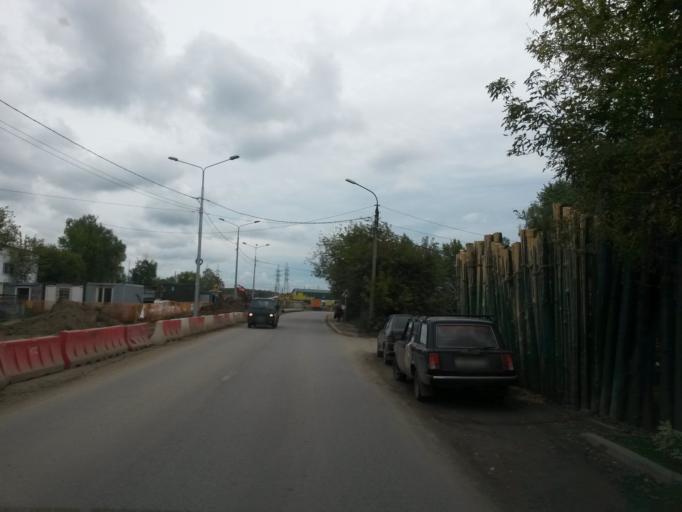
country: RU
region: Moskovskaya
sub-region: Chekhovskiy Rayon
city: Chekhov
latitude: 55.1414
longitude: 37.4779
